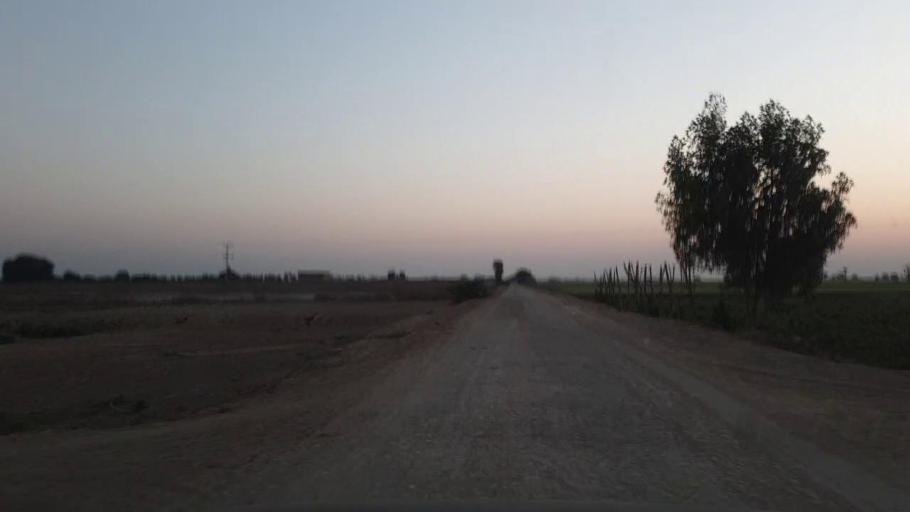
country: PK
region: Sindh
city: Digri
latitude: 25.1917
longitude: 69.1897
